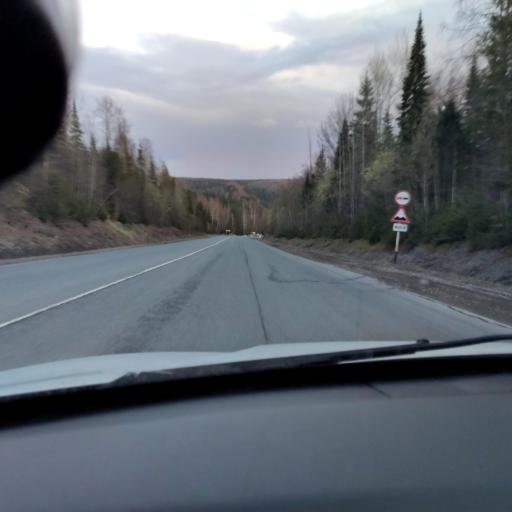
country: RU
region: Perm
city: Gremyachinsk
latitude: 58.4492
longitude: 57.8722
